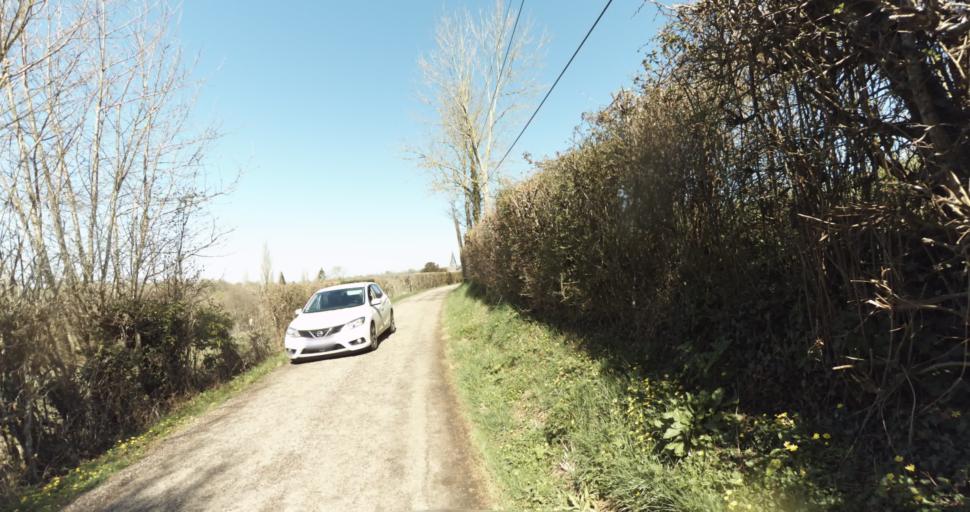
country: FR
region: Lower Normandy
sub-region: Departement du Calvados
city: Livarot
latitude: 48.9974
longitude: 0.0971
